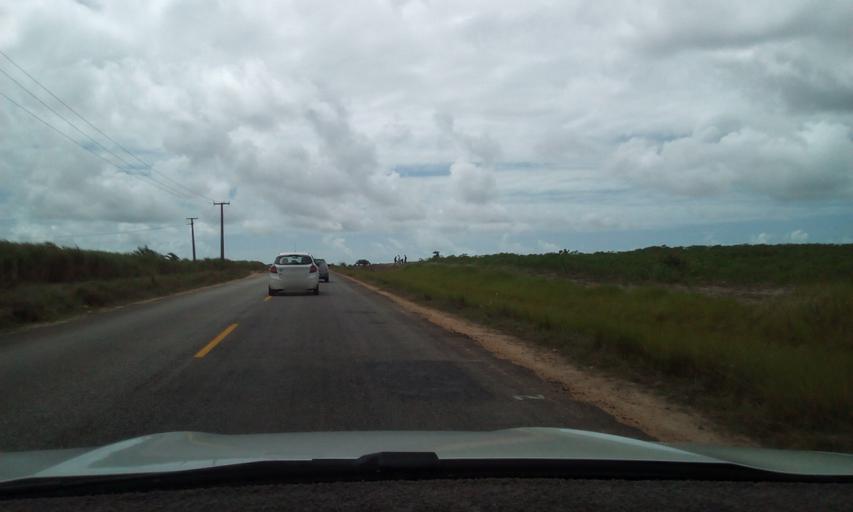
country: BR
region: Paraiba
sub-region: Rio Tinto
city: Rio Tinto
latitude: -6.7810
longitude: -35.0543
